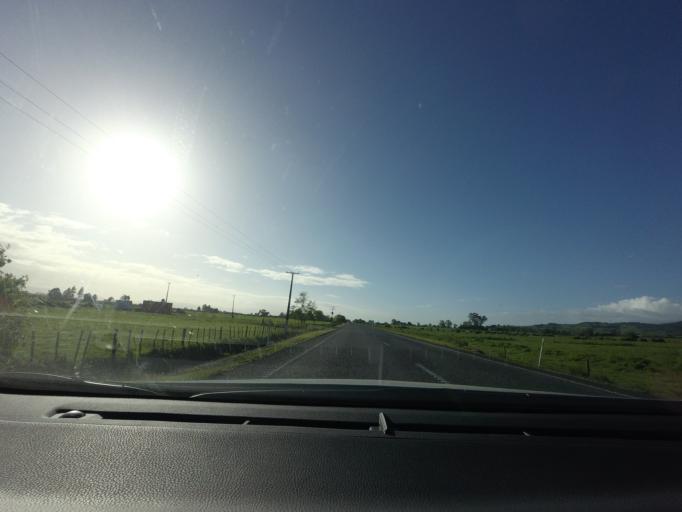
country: NZ
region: Waikato
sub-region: Hauraki District
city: Ngatea
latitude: -37.3911
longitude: 175.4572
